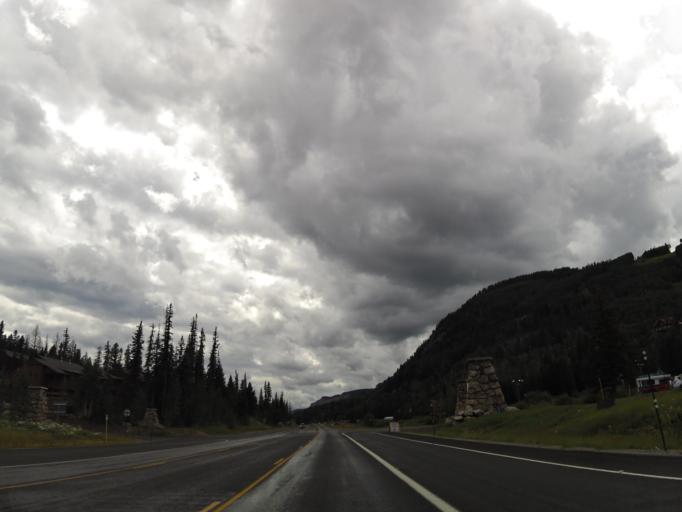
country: US
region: Colorado
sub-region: San Juan County
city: Silverton
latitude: 37.6289
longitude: -107.8097
